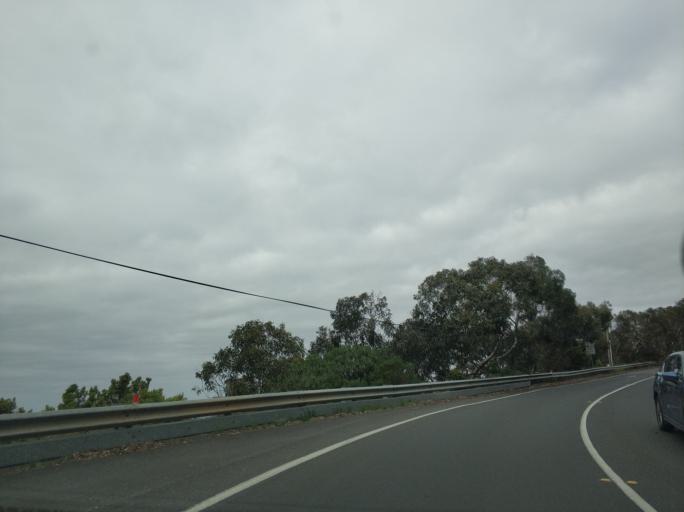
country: AU
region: Victoria
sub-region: Surf Coast
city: Anglesea
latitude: -38.4862
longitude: 144.0289
